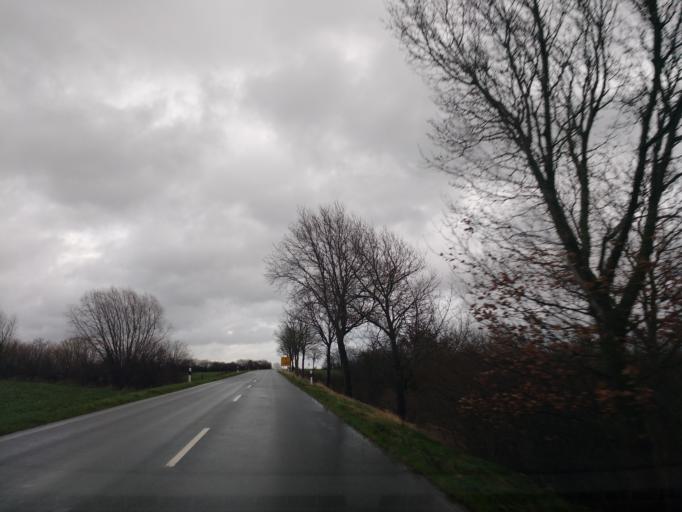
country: DE
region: Schleswig-Holstein
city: Blekendorf
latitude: 54.2965
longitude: 10.6734
